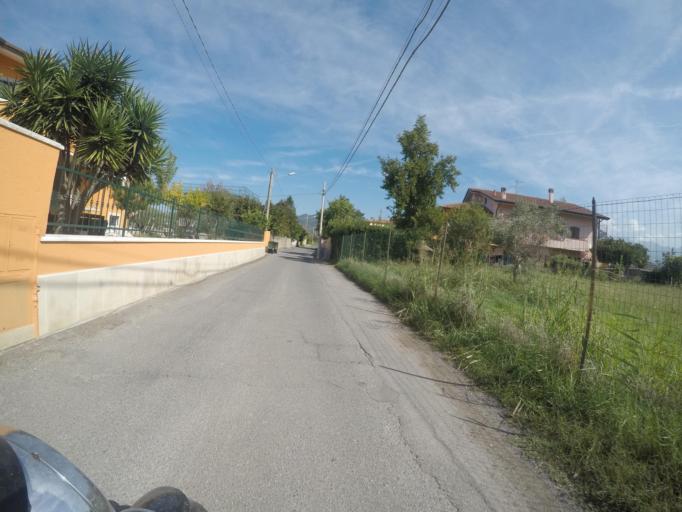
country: IT
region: Liguria
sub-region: Provincia di La Spezia
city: Casano-Dogana-Isola
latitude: 44.0564
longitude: 10.0321
